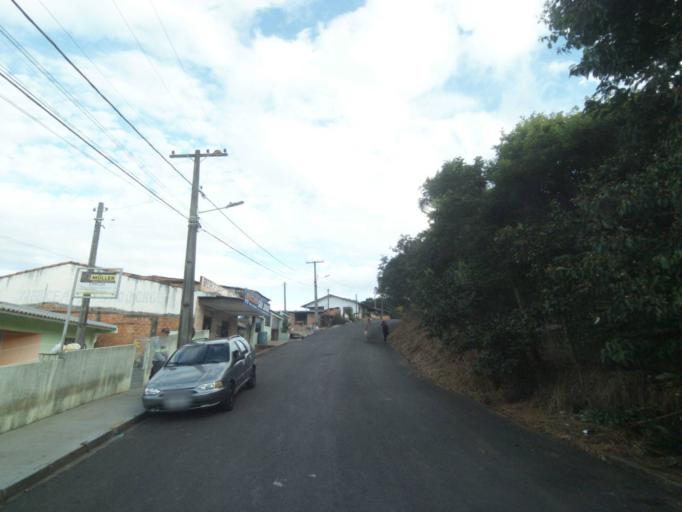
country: BR
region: Parana
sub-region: Telemaco Borba
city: Telemaco Borba
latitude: -24.3271
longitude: -50.6082
